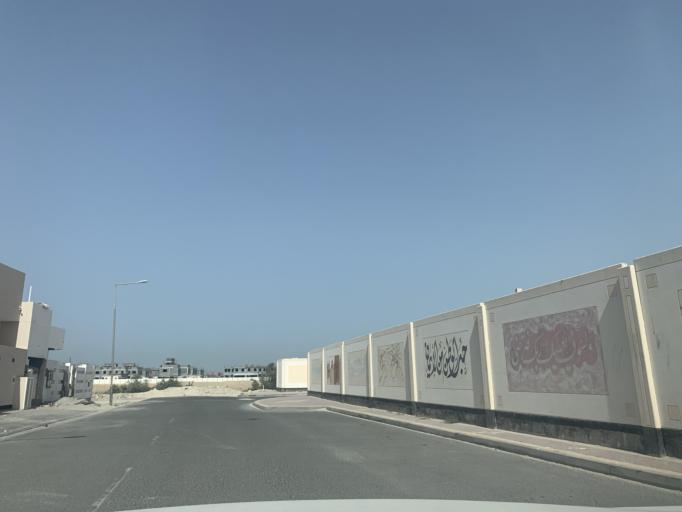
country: BH
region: Northern
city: Sitrah
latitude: 26.1655
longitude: 50.6286
